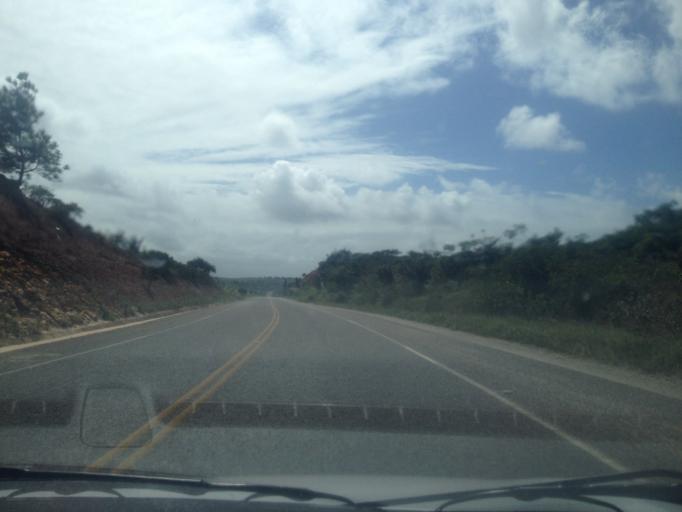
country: BR
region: Bahia
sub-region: Conde
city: Conde
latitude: -11.9058
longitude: -37.6530
